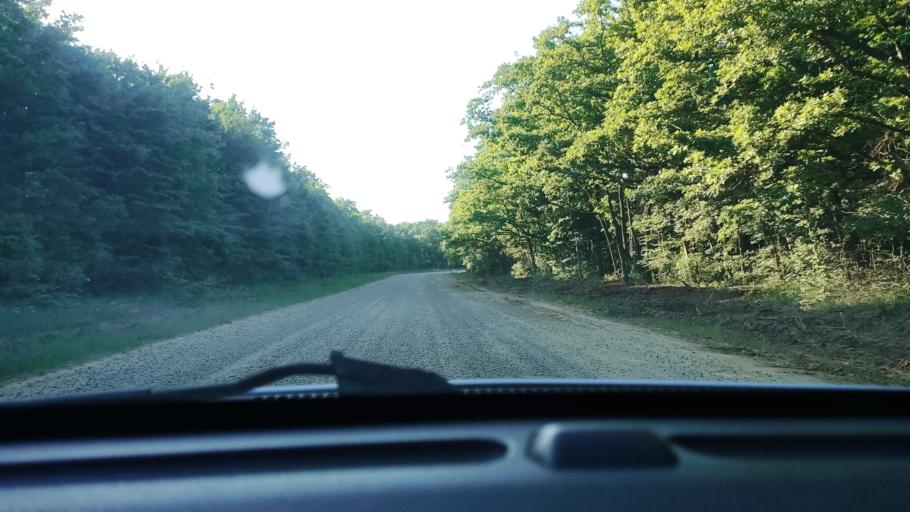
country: RU
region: Krasnodarskiy
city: Novodmitriyevskaya
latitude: 44.7192
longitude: 38.9911
